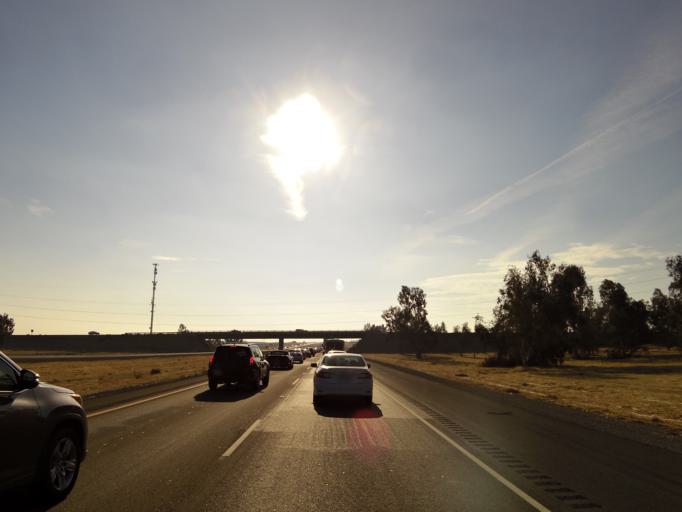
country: US
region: California
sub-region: Fresno County
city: Mendota
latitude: 36.6408
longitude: -120.6240
